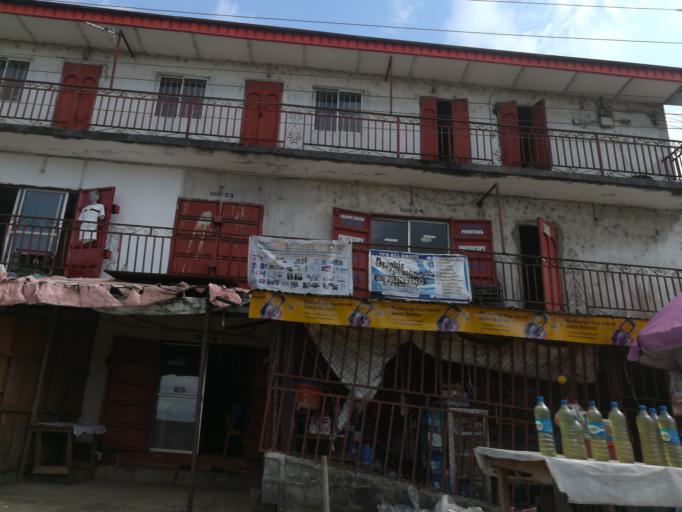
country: NG
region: Rivers
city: Okrika
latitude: 4.7495
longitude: 7.1063
